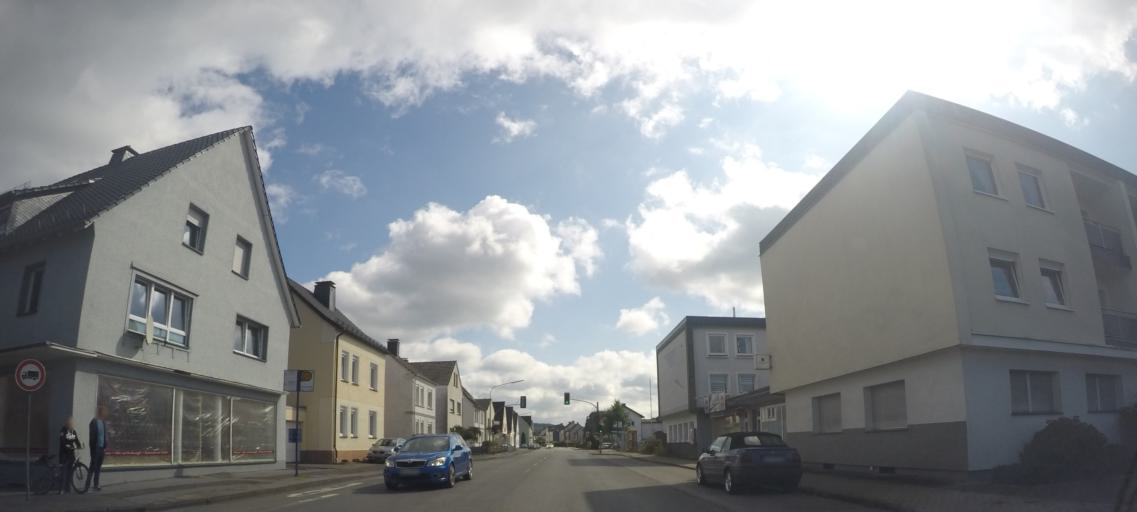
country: DE
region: North Rhine-Westphalia
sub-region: Regierungsbezirk Arnsberg
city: Arnsberg
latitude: 51.4251
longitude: 8.0182
